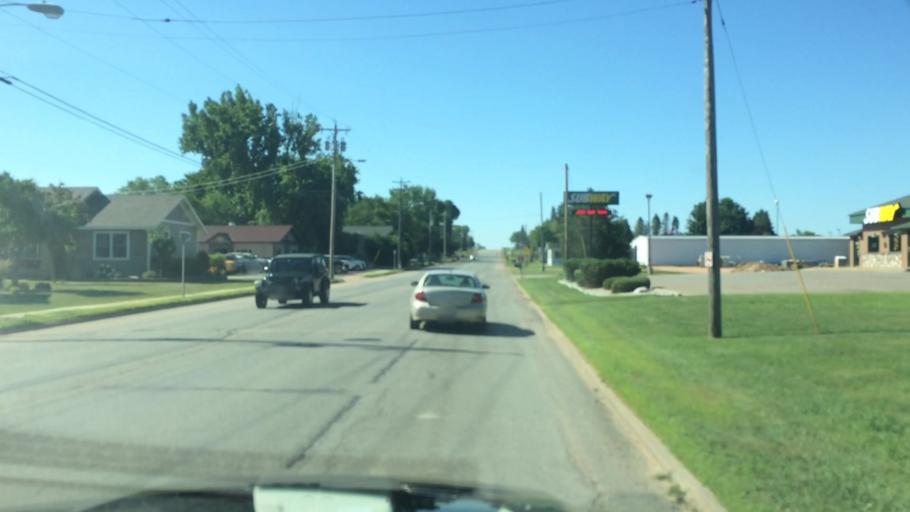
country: US
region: Wisconsin
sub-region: Marathon County
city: Stratford
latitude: 44.7974
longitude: -90.0792
